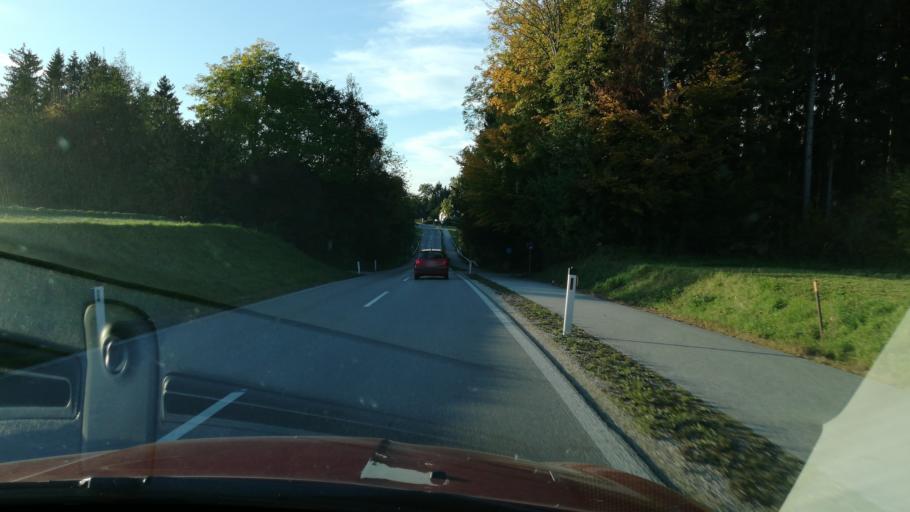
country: AT
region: Upper Austria
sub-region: Politischer Bezirk Steyr-Land
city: Waldneukirchen
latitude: 48.0162
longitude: 14.2408
